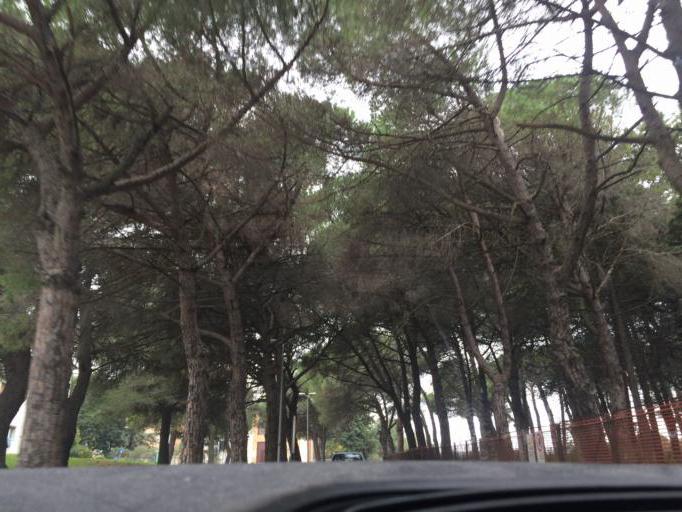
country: IT
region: Basilicate
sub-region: Provincia di Matera
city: Matera
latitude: 40.6608
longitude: 16.6019
